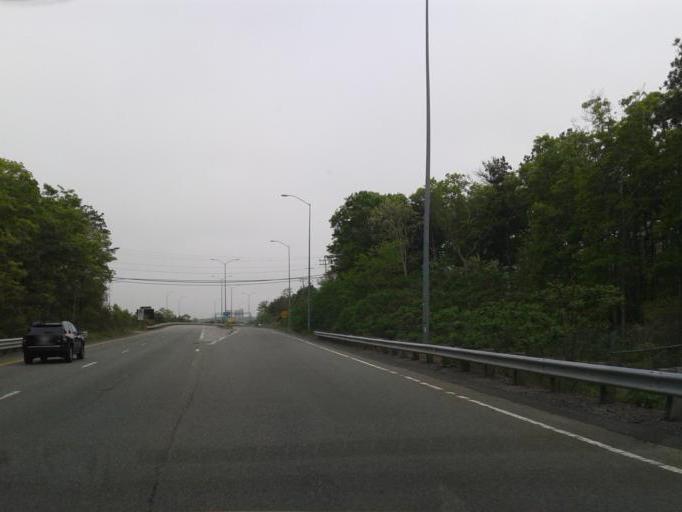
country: US
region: Massachusetts
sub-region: Barnstable County
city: Sagamore
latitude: 41.7868
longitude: -70.5450
